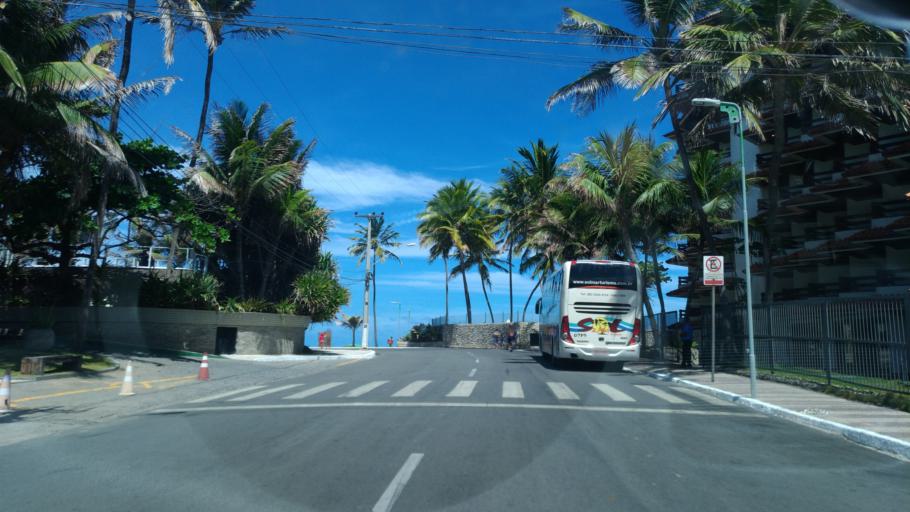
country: BR
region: Alagoas
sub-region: Maceio
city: Maceio
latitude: -9.6396
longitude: -35.6991
